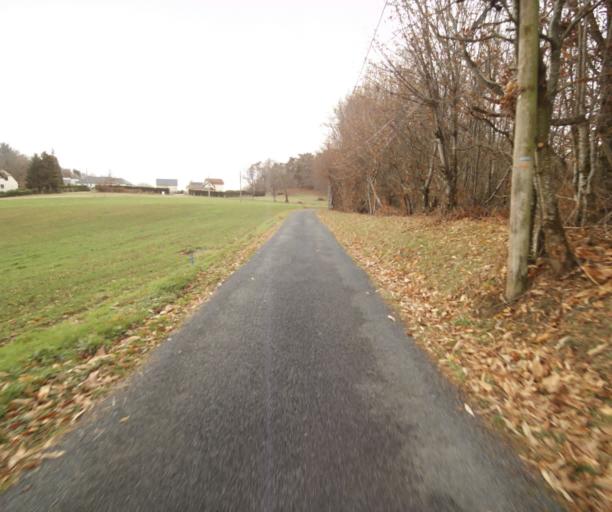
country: FR
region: Limousin
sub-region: Departement de la Correze
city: Chameyrat
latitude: 45.2676
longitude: 1.6970
